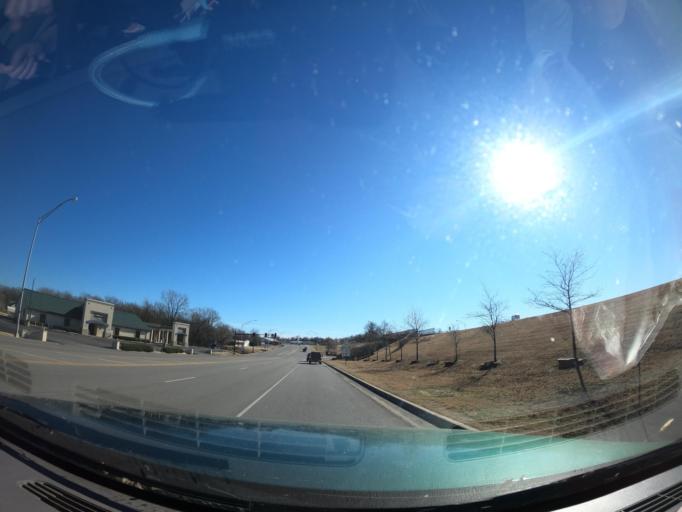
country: US
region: Oklahoma
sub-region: Wagoner County
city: Coweta
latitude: 35.9569
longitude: -95.6503
